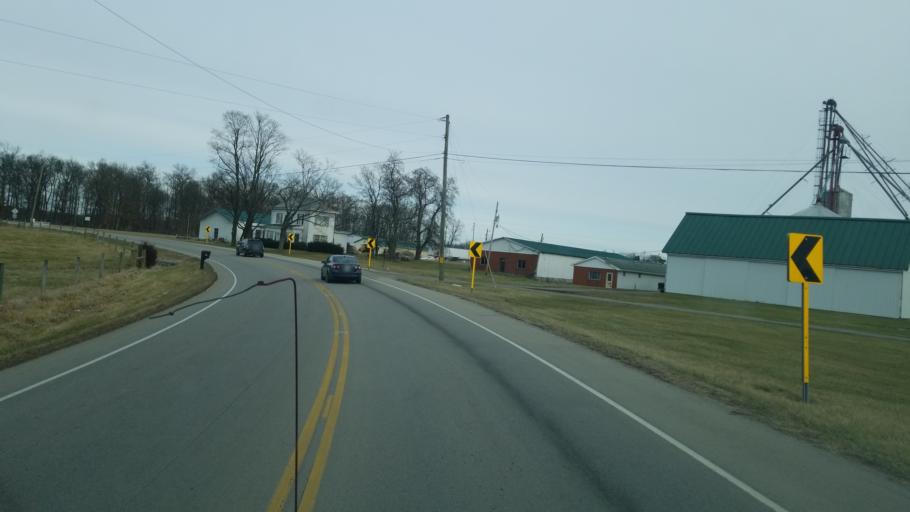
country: US
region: Ohio
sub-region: Adams County
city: Winchester
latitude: 39.0642
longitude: -83.6908
